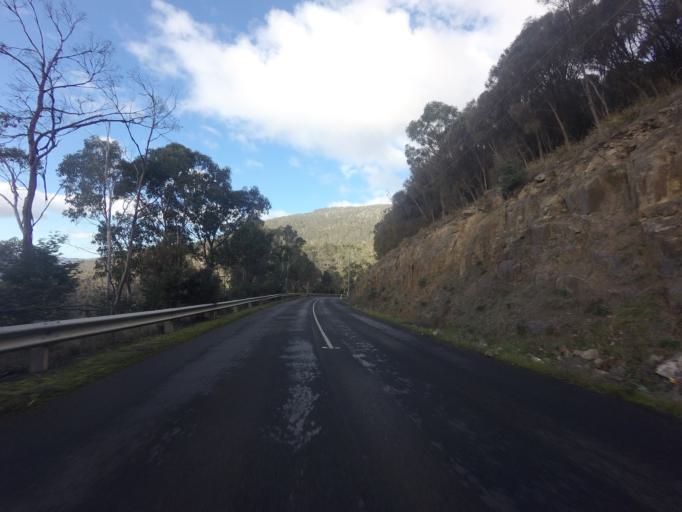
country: AU
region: Tasmania
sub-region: Glenorchy
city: Berriedale
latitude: -42.8232
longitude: 147.2064
